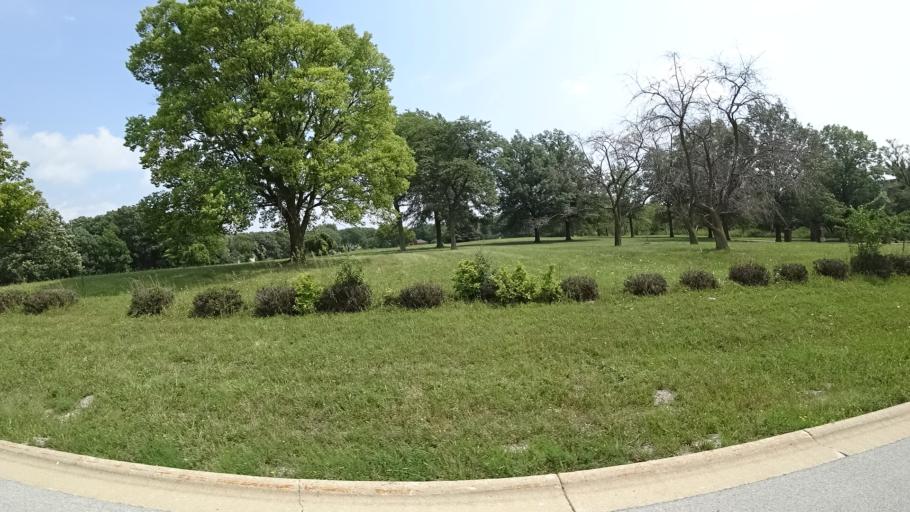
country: US
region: Illinois
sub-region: Cook County
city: Orland Park
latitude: 41.6324
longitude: -87.8828
